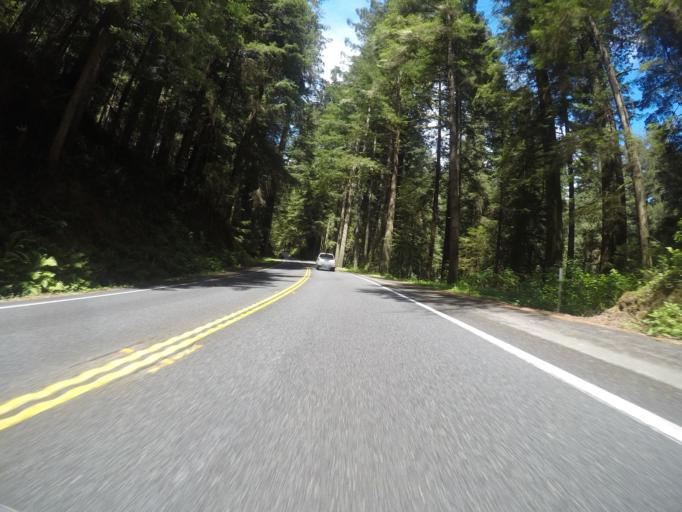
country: US
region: California
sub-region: Del Norte County
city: Bertsch-Oceanview
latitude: 41.8105
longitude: -124.1223
